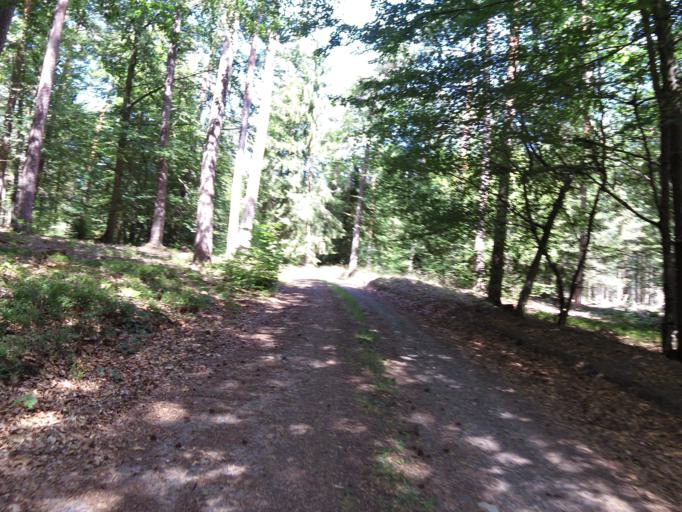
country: DE
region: Rheinland-Pfalz
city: Carlsberg
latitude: 49.4783
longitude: 8.0103
